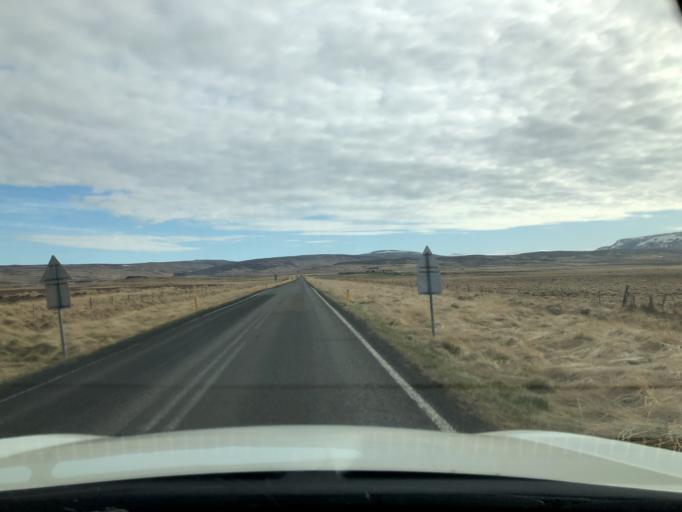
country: IS
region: West
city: Borgarnes
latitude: 65.0255
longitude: -21.7509
